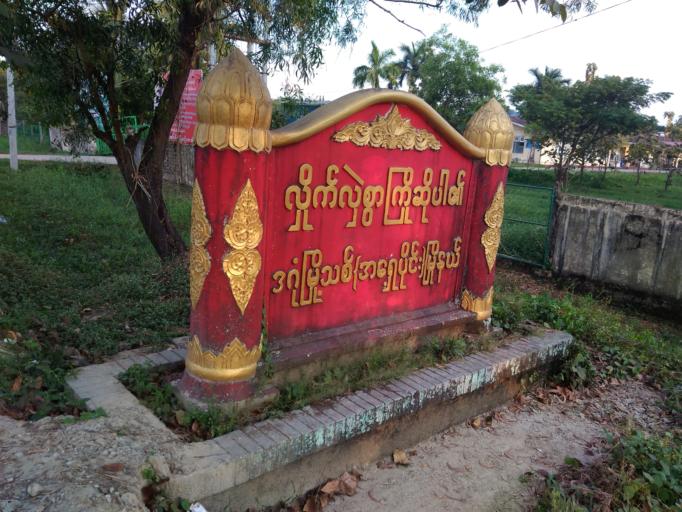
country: MM
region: Yangon
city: Yangon
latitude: 16.8919
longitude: 96.1984
